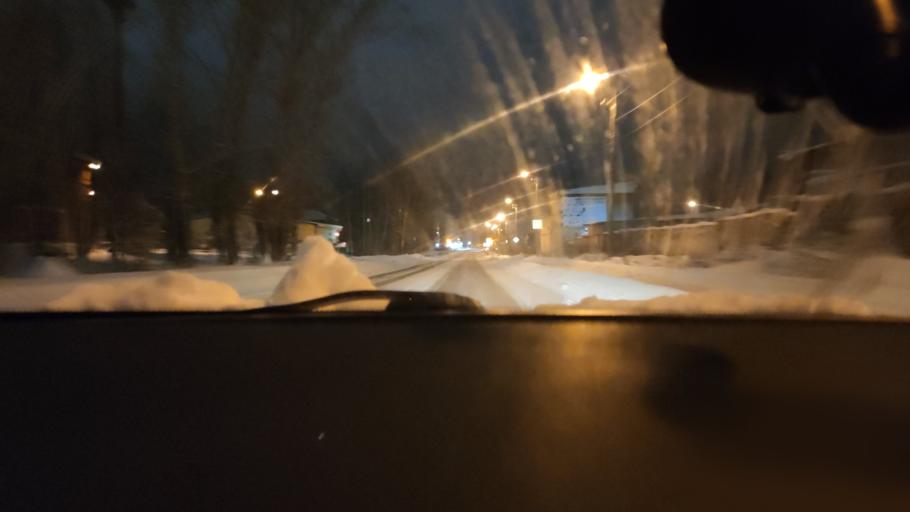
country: RU
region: Perm
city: Krasnokamsk
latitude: 58.0836
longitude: 55.7675
